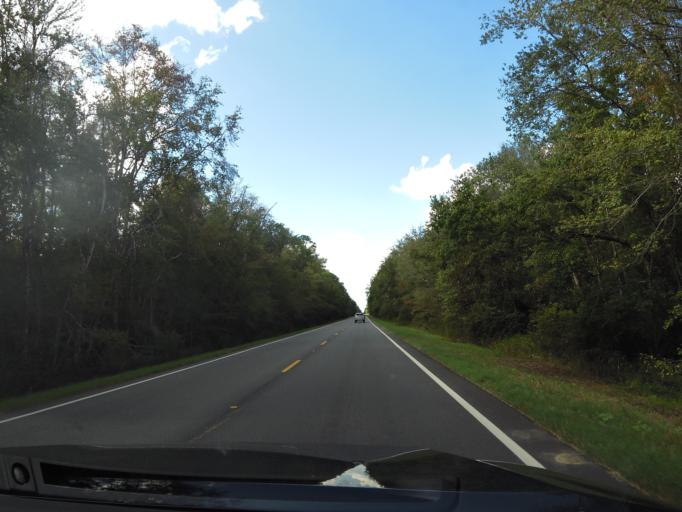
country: US
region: Georgia
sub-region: Echols County
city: Statenville
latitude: 30.7315
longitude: -83.0856
